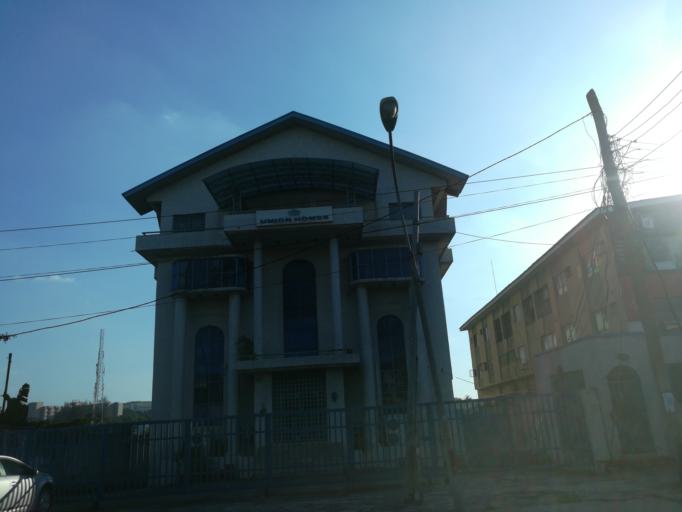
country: NG
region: Lagos
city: Ojota
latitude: 6.5883
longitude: 3.3622
